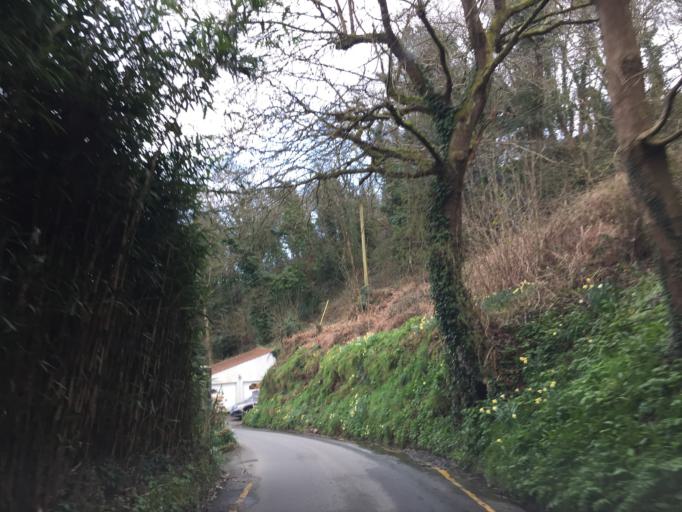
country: JE
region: St Helier
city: Saint Helier
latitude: 49.2099
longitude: -2.1546
